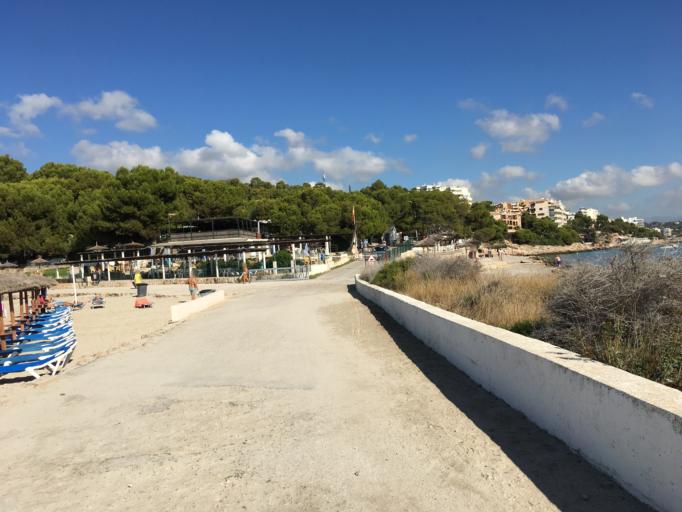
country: ES
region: Balearic Islands
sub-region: Illes Balears
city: Magaluf
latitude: 39.5330
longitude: 2.5893
